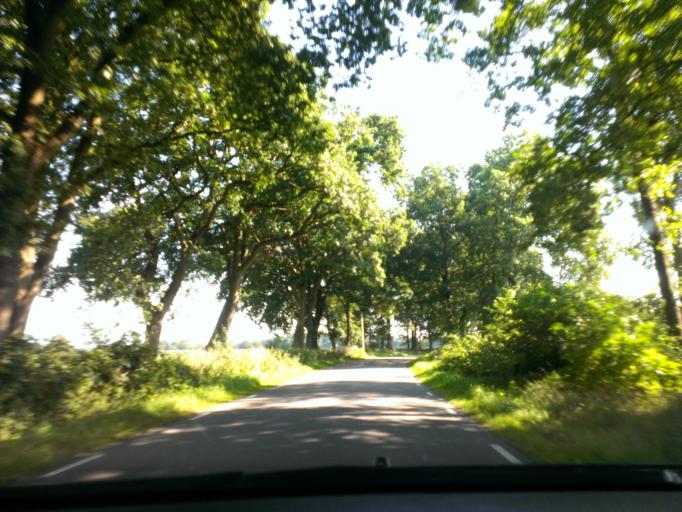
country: NL
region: Drenthe
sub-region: Gemeente Coevorden
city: Dalen
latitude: 52.6795
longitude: 6.7605
